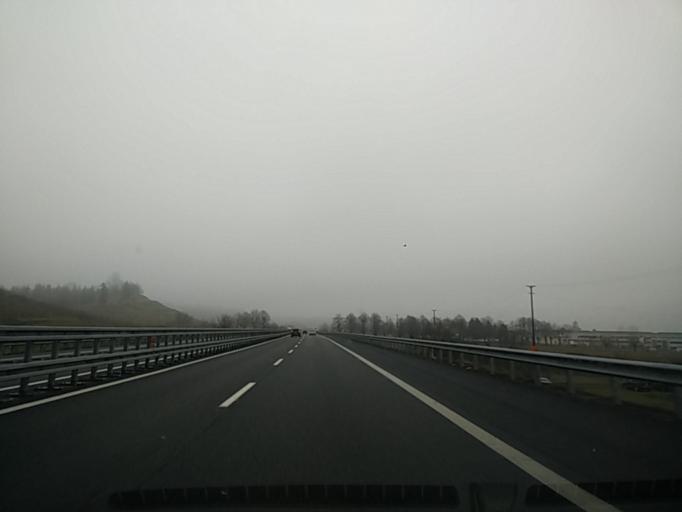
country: IT
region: Piedmont
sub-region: Provincia di Asti
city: Azzano d'Asti
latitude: 44.9082
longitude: 8.2636
